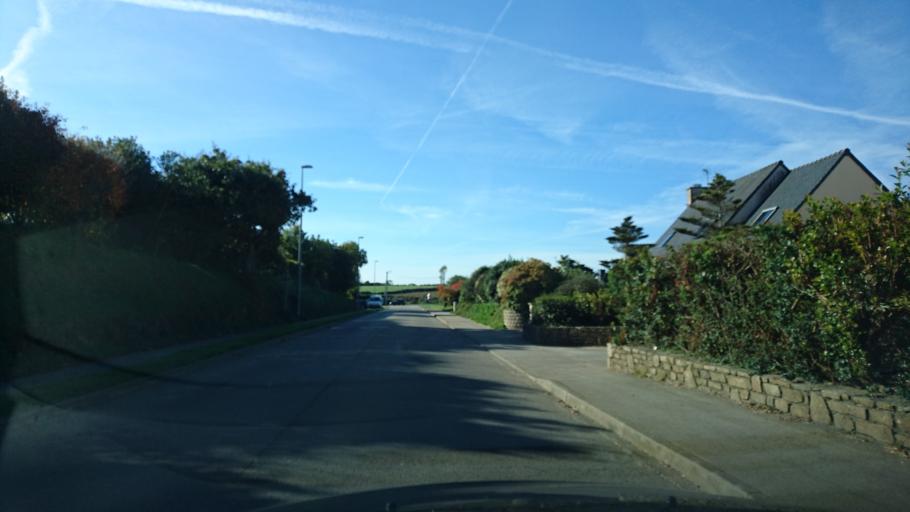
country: FR
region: Brittany
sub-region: Departement du Finistere
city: Saint-Renan
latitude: 48.4316
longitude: -4.6319
